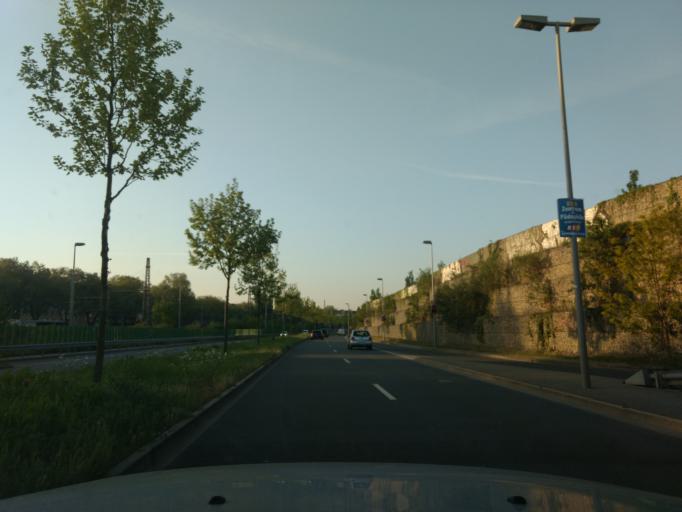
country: DE
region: North Rhine-Westphalia
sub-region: Regierungsbezirk Dusseldorf
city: Dusseldorf
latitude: 51.2424
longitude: 6.7956
